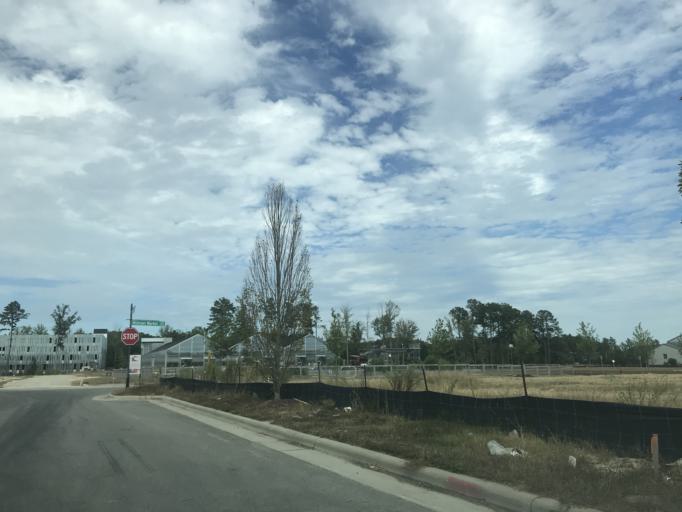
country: US
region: North Carolina
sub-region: Wake County
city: Knightdale
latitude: 35.8633
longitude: -78.5401
